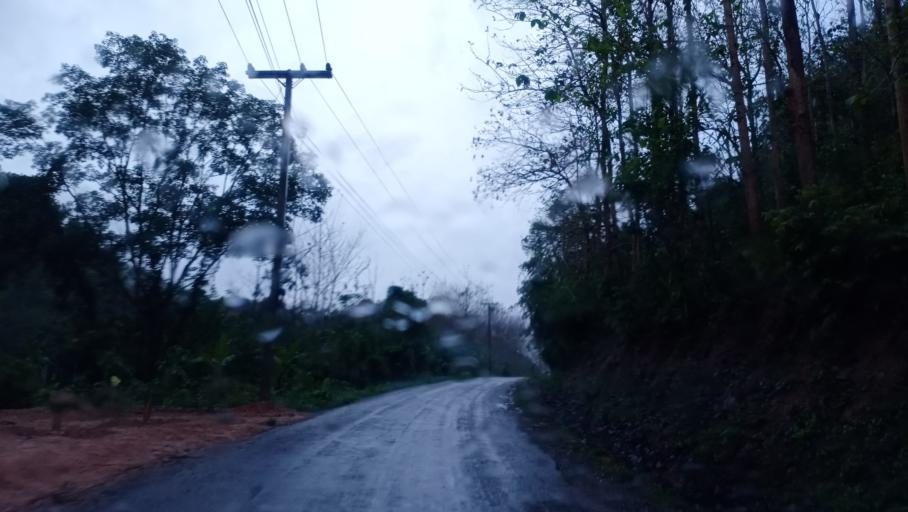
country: LA
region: Phongsali
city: Khoa
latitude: 21.0626
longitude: 102.4746
